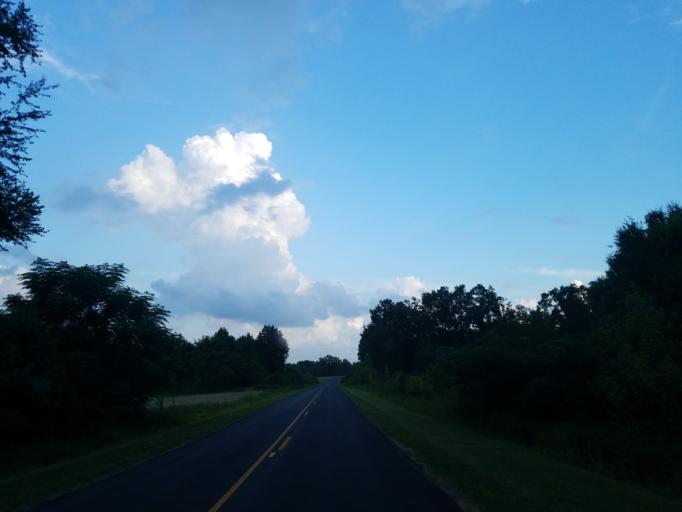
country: US
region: Georgia
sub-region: Dooly County
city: Unadilla
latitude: 32.1894
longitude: -83.7569
